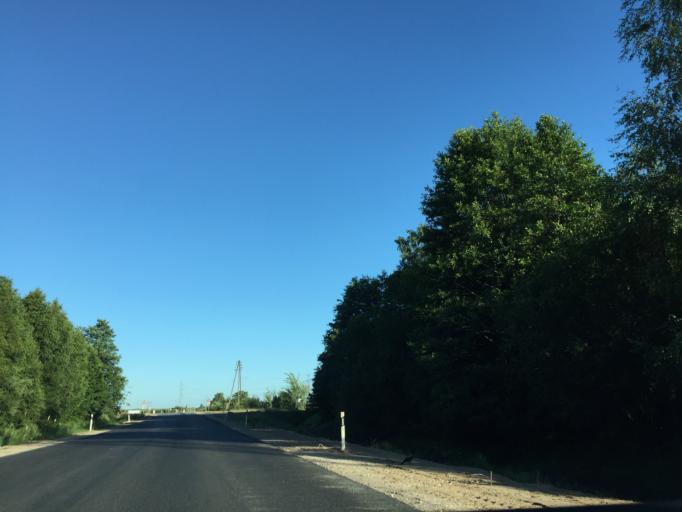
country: LV
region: Ventspils
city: Ventspils
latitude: 57.3956
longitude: 21.6350
